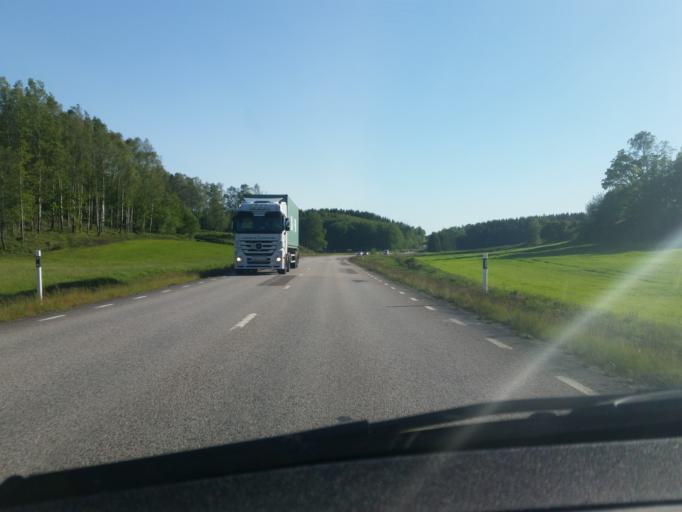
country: SE
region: Vaestra Goetaland
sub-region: Fargelanda Kommun
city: Faergelanda
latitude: 58.5836
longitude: 12.0255
